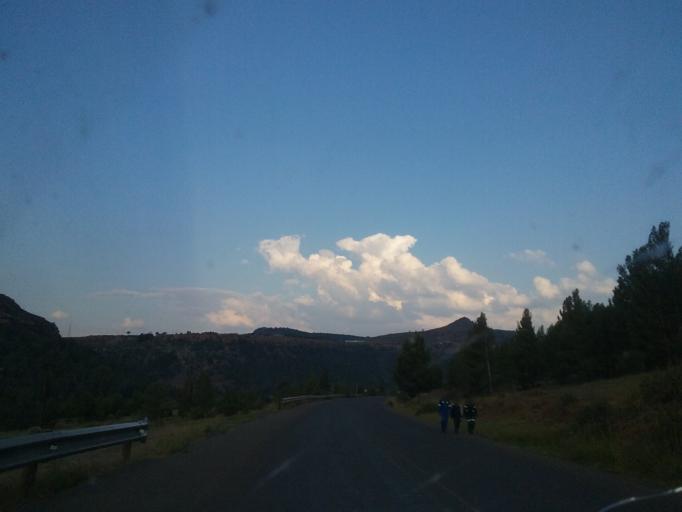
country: LS
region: Quthing
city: Quthing
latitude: -30.3994
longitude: 27.6717
